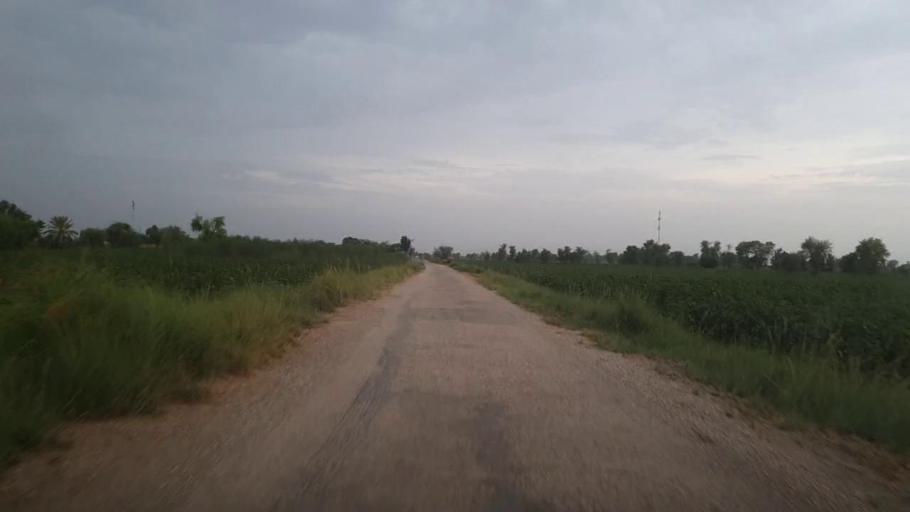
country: PK
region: Sindh
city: Karaundi
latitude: 27.0066
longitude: 68.3438
